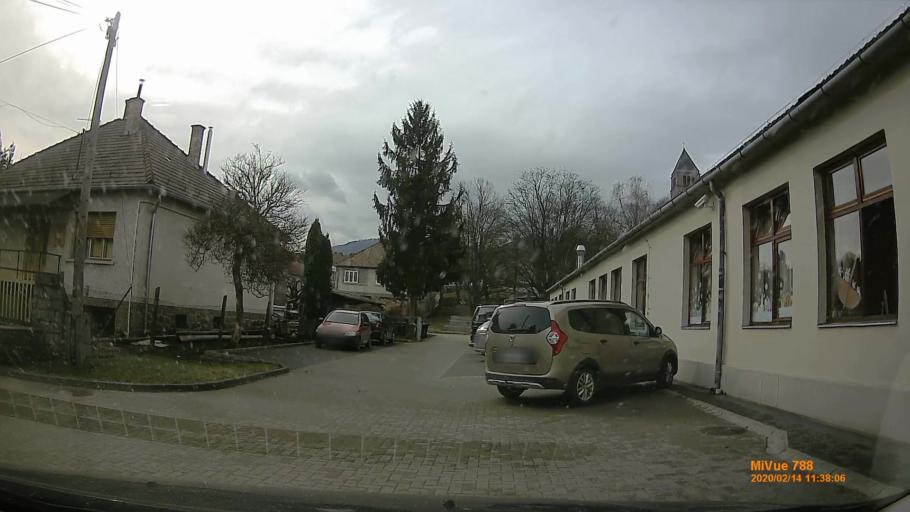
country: HU
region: Pest
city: Dunabogdany
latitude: 47.7925
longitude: 19.0345
